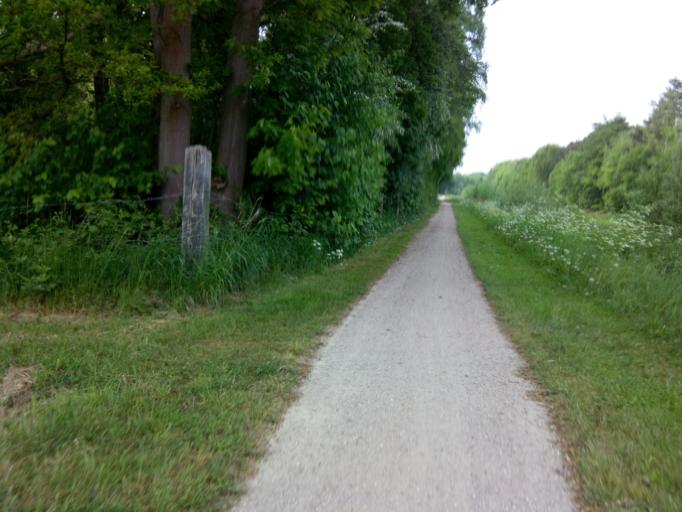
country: NL
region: Gelderland
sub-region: Berkelland
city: Borculo
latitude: 52.0844
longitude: 6.5116
